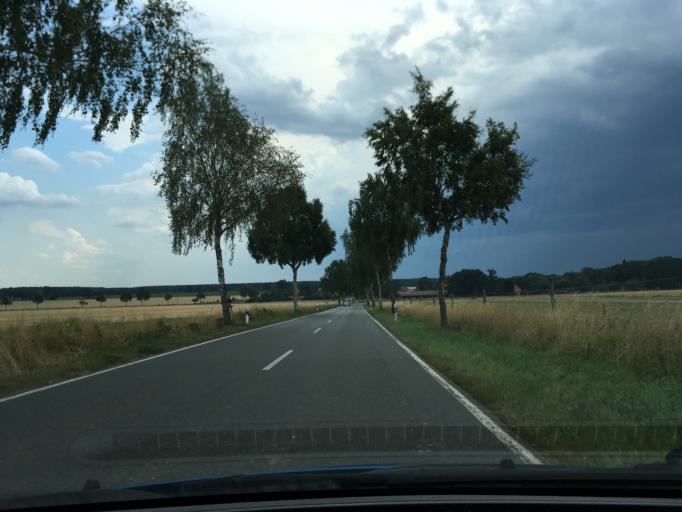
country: DE
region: Lower Saxony
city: Barnstedt
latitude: 53.0982
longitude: 10.3988
